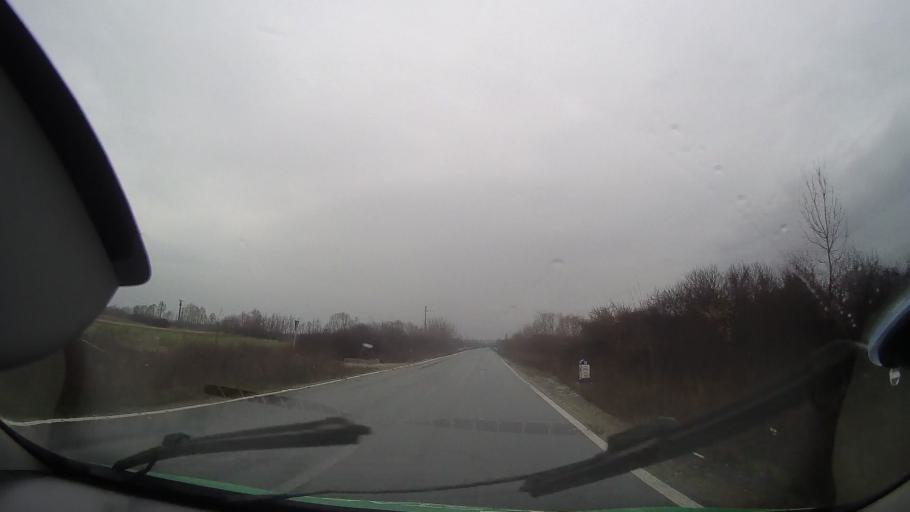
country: RO
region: Bihor
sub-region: Comuna Tinca
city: Tinca
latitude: 46.7401
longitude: 21.9406
